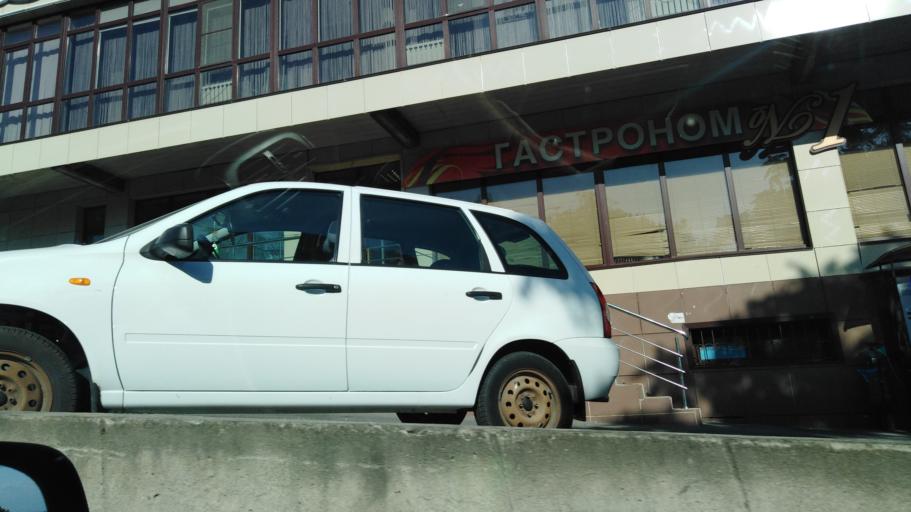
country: RU
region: Stavropol'skiy
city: Pyatigorsk
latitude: 44.0481
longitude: 43.0686
